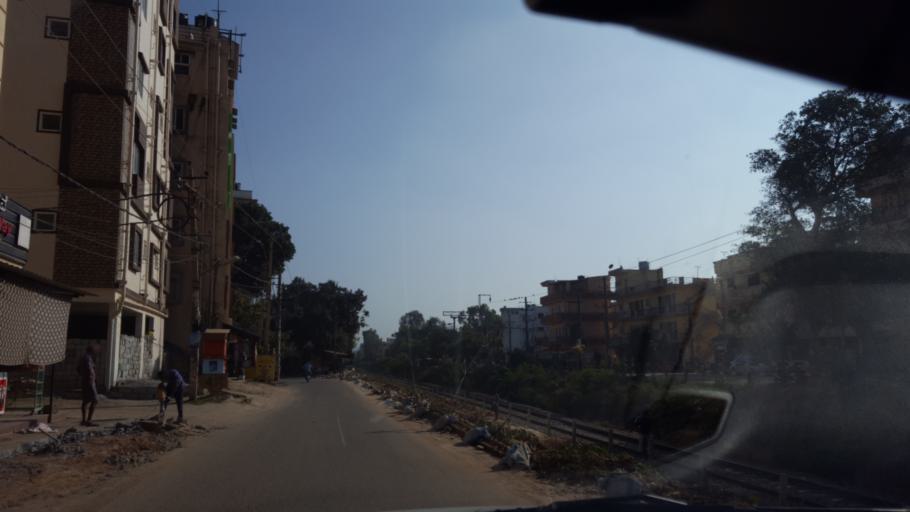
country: IN
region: Karnataka
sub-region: Bangalore Urban
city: Bangalore
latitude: 12.9549
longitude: 77.7050
